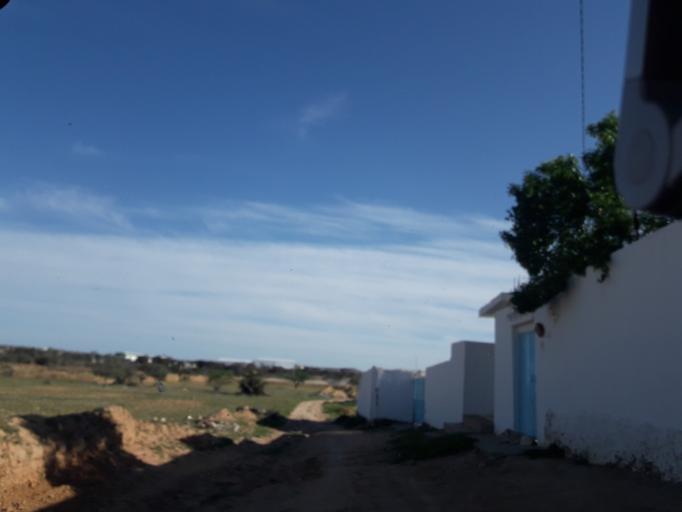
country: TN
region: Safaqis
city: Sfax
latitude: 34.7369
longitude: 10.5174
